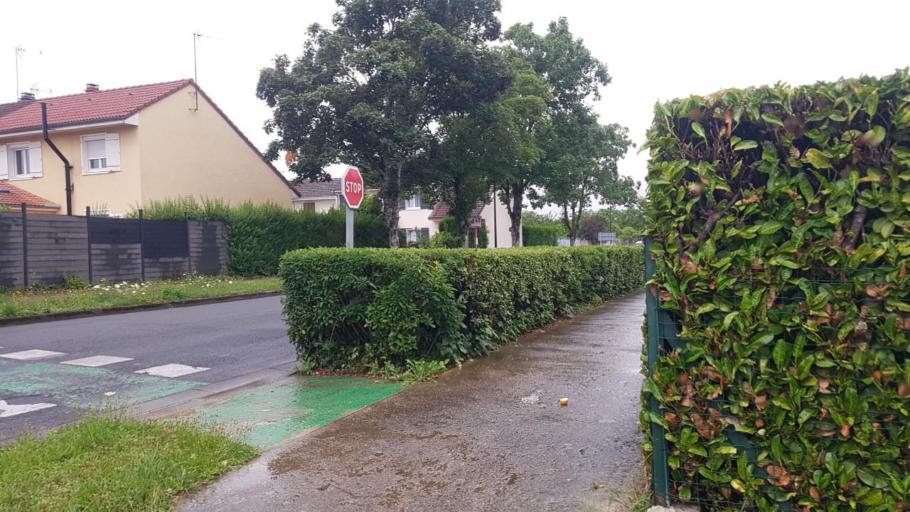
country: FR
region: Champagne-Ardenne
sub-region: Departement de la Marne
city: Vitry-le-Francois
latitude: 48.7334
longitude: 4.5965
